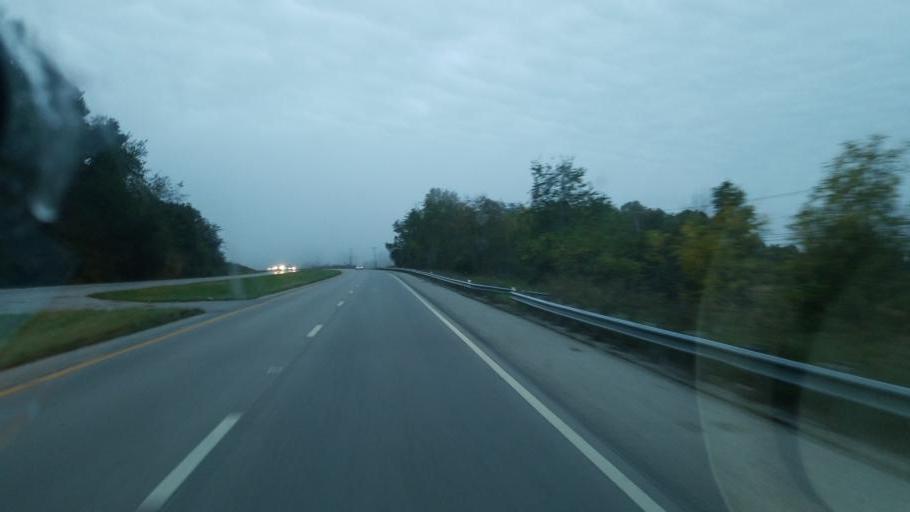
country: US
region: Ohio
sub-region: Scioto County
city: Lucasville
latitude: 38.9627
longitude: -83.0243
